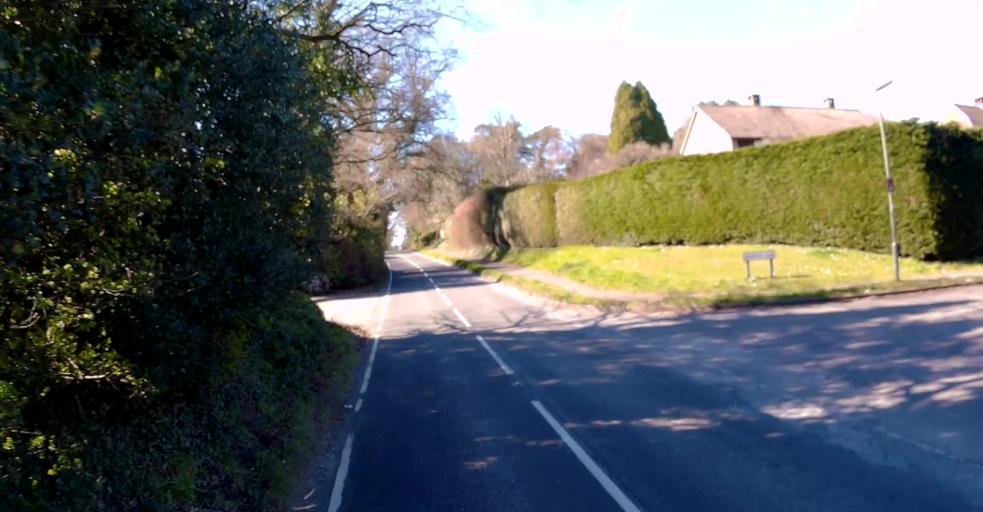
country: GB
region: England
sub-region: Surrey
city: Farnham
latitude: 51.2055
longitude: -0.7811
